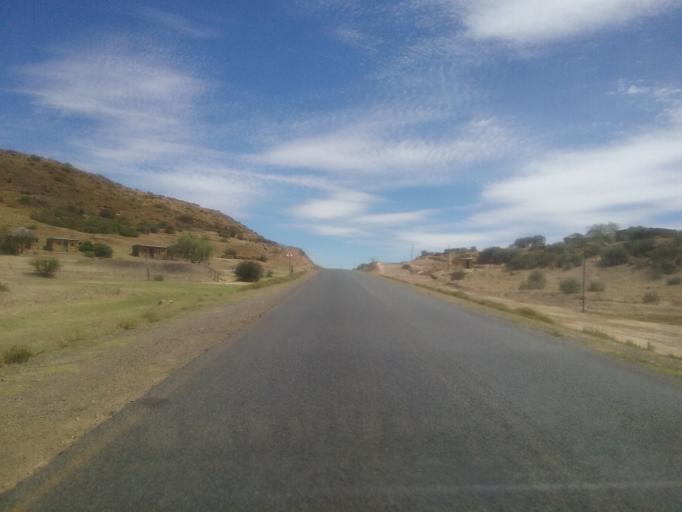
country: LS
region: Mohale's Hoek District
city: Mohale's Hoek
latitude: -30.0675
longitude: 27.4214
